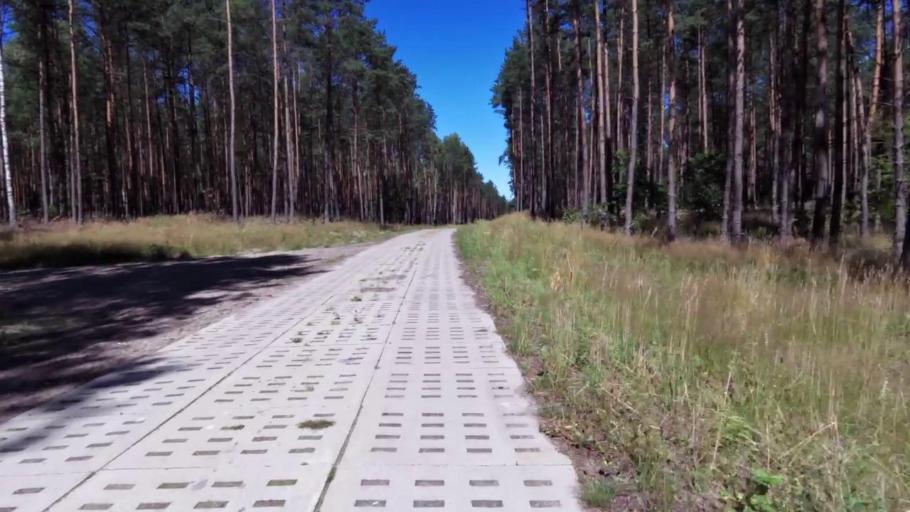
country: PL
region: West Pomeranian Voivodeship
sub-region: Powiat szczecinecki
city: Szczecinek
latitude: 53.6223
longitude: 16.6617
